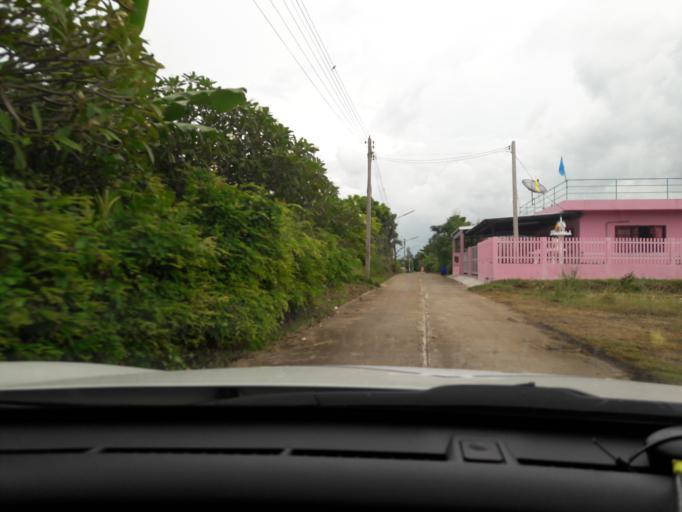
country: TH
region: Nakhon Sawan
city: Tak Fa
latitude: 15.3539
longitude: 100.4982
